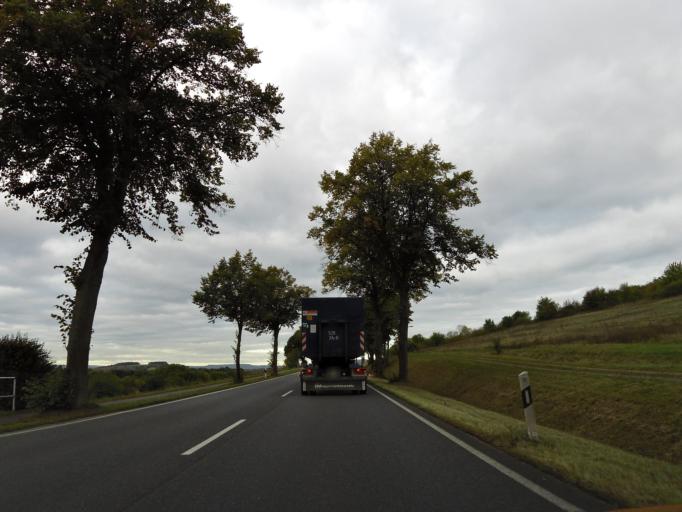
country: DE
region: Lower Saxony
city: Northeim
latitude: 51.7694
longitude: 9.9502
